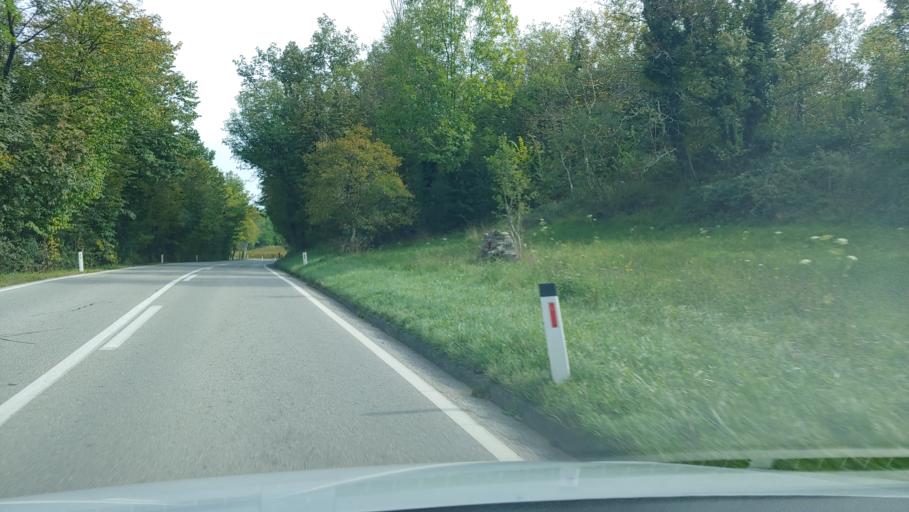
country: SI
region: Nova Gorica
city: Sempas
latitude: 45.9158
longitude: 13.7648
